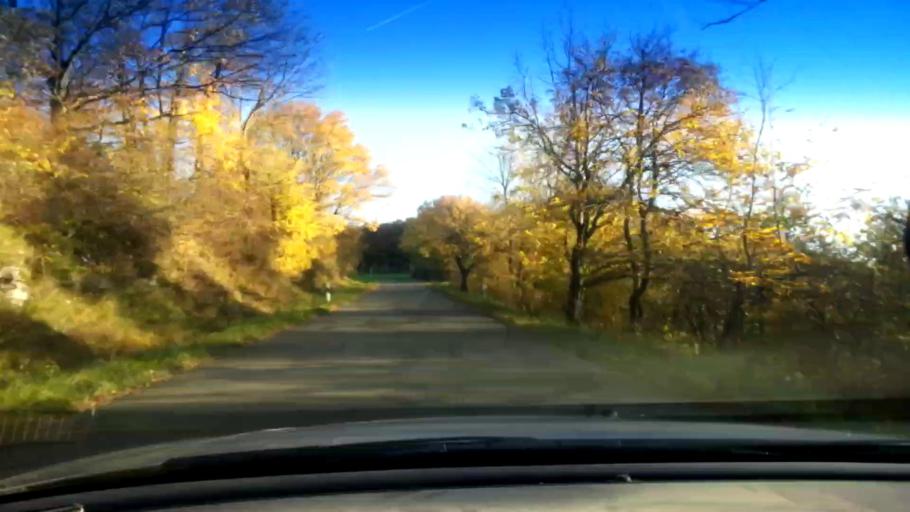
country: DE
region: Bavaria
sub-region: Upper Franconia
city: Heiligenstadt
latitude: 49.8661
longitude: 11.1799
